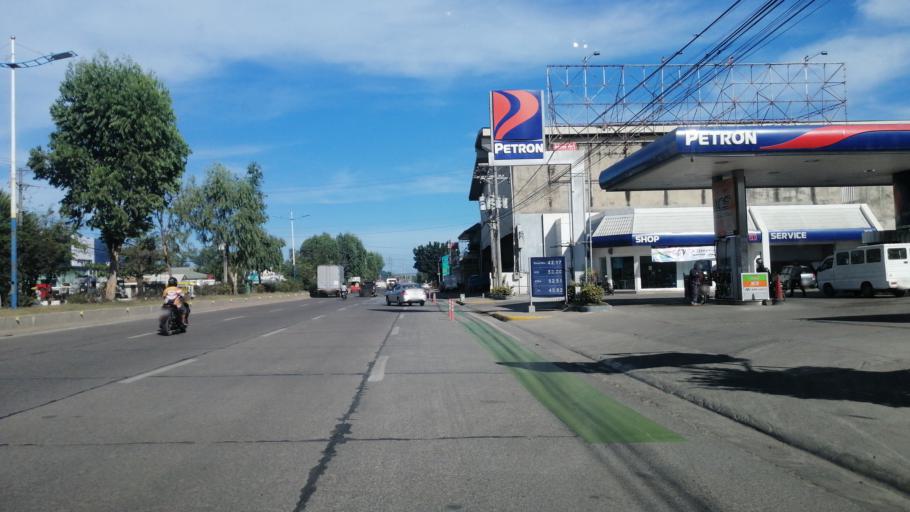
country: PH
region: Central Visayas
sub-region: Lapu-Lapu City
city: Buagsong
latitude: 10.3254
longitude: 123.9387
